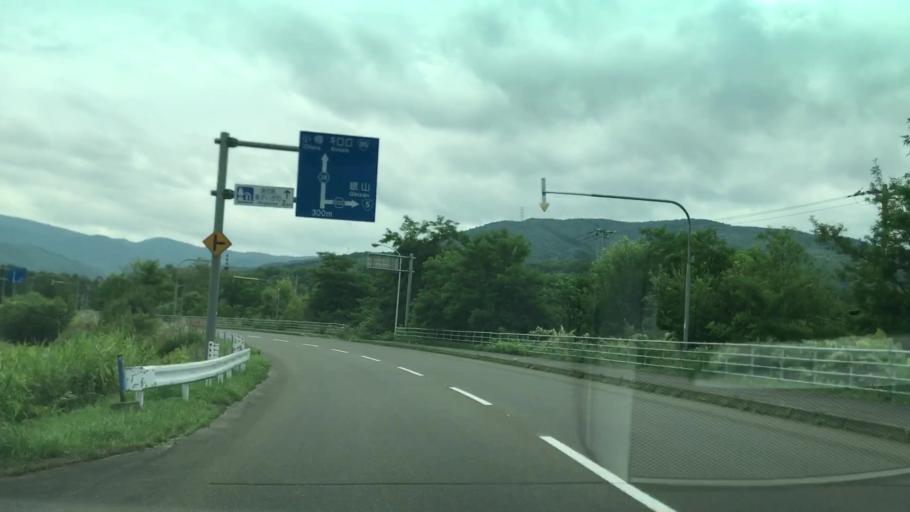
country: JP
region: Hokkaido
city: Yoichi
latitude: 43.0514
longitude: 140.8209
